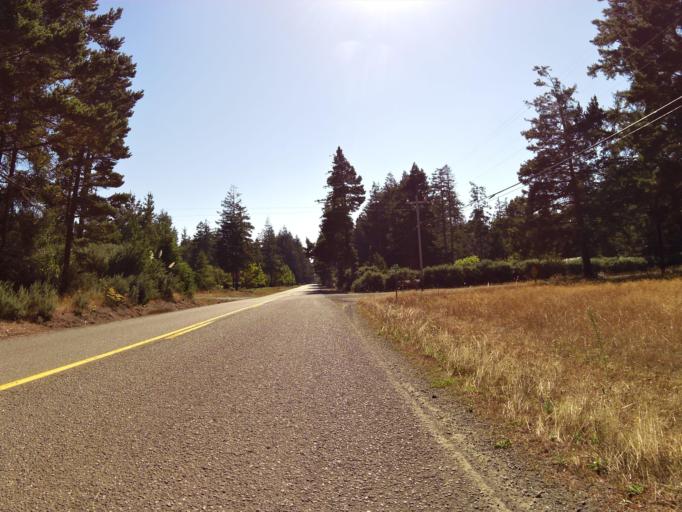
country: US
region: Oregon
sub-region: Coos County
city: Bandon
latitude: 43.1841
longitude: -124.3685
